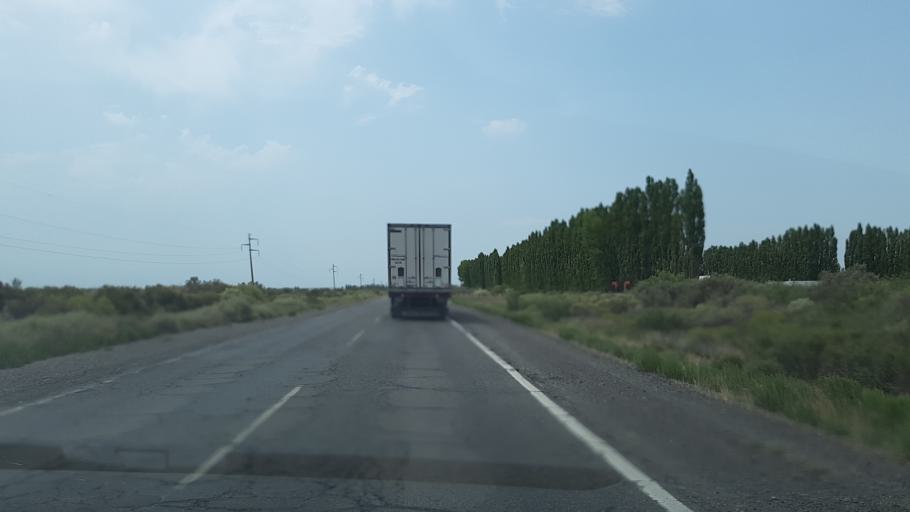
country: AR
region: Rio Negro
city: Catriel
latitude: -37.9429
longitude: -67.8862
